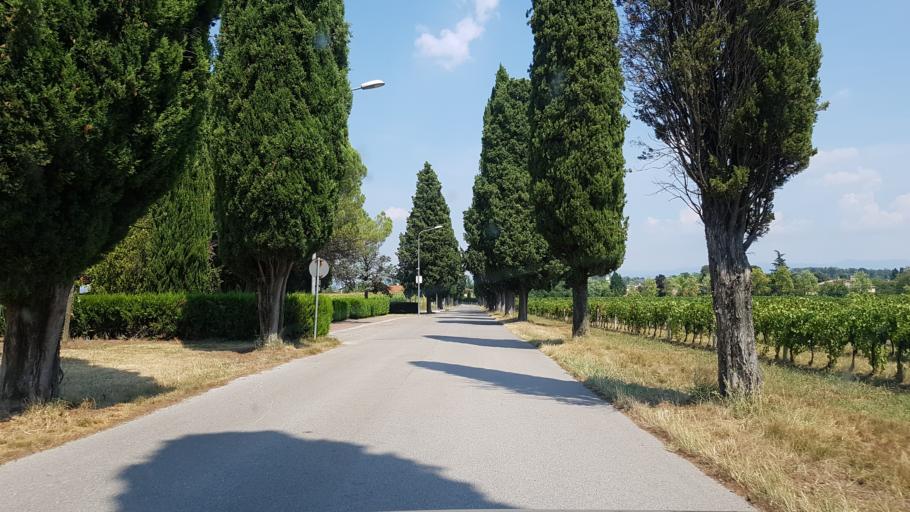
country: IT
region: Friuli Venezia Giulia
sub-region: Provincia di Gorizia
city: Farra d'Isonzo
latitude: 45.9043
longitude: 13.5094
